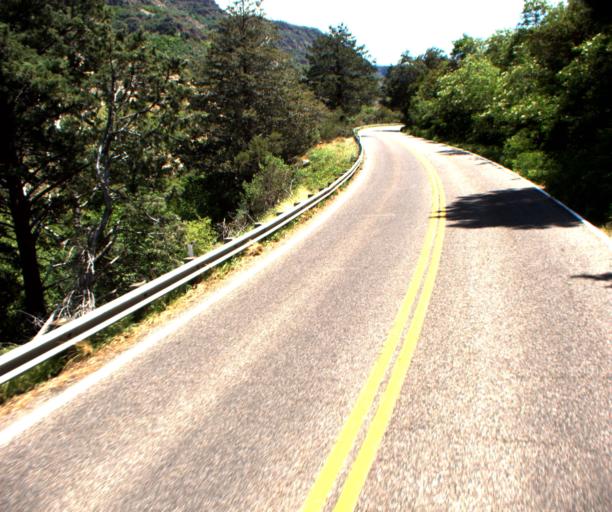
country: US
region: Arizona
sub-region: Coconino County
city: Sedona
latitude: 34.9408
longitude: -111.7509
